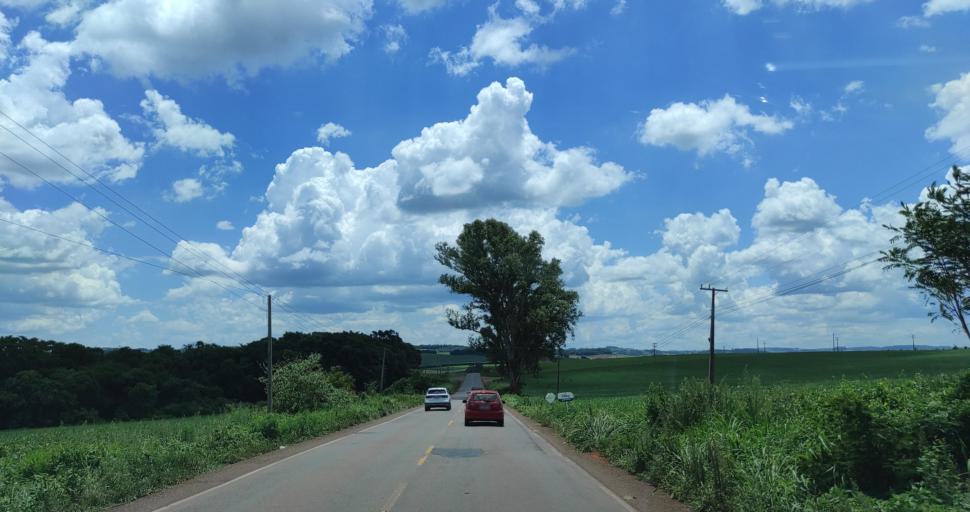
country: BR
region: Santa Catarina
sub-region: Xanxere
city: Xanxere
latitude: -26.7584
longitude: -52.4034
